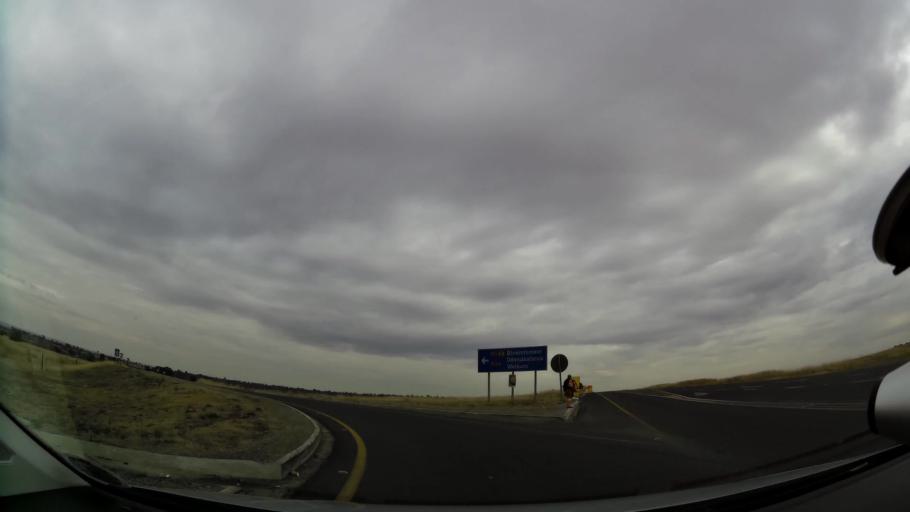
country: ZA
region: Orange Free State
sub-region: Fezile Dabi District Municipality
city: Kroonstad
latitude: -27.6249
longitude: 27.2562
